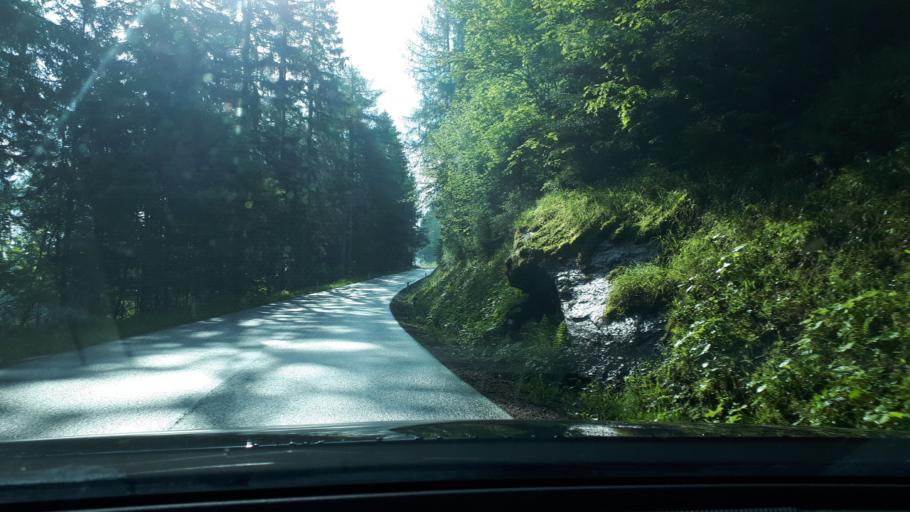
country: AT
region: Styria
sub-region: Politischer Bezirk Voitsberg
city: Modriach
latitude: 46.9264
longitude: 15.0119
